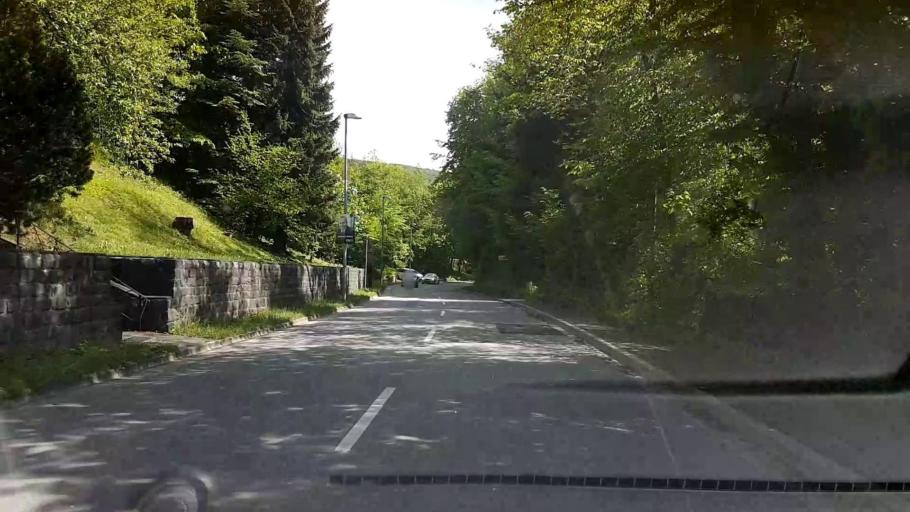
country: DE
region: Bavaria
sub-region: Upper Franconia
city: Ebermannstadt
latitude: 49.7873
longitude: 11.1804
